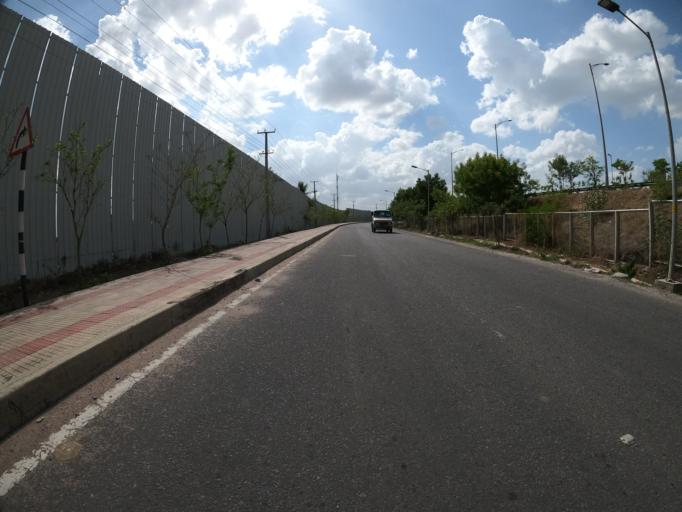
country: IN
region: Telangana
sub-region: Hyderabad
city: Hyderabad
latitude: 17.3943
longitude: 78.3494
